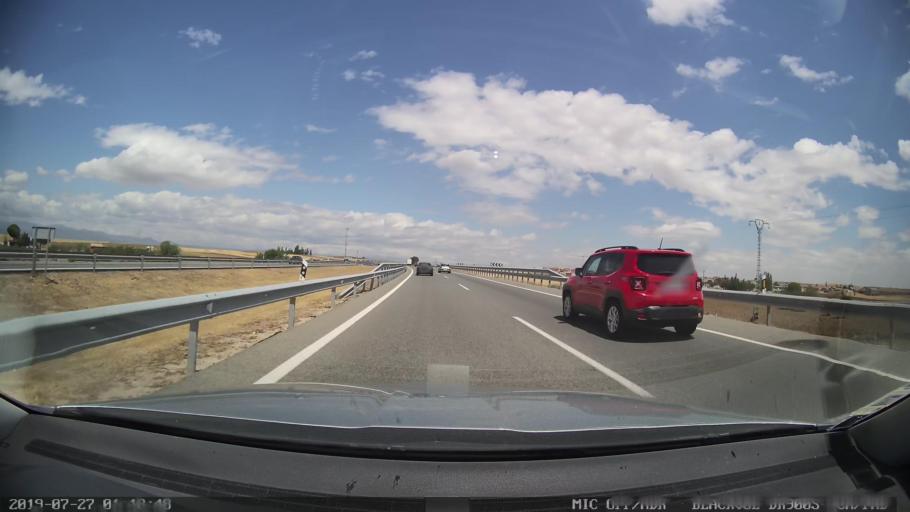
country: ES
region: Castille-La Mancha
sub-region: Province of Toledo
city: Quismondo
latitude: 40.1013
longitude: -4.3346
